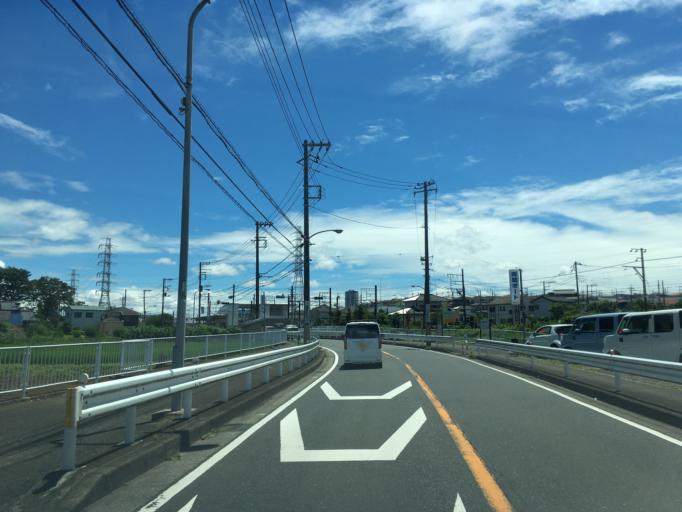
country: JP
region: Tokyo
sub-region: Machida-shi
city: Machida
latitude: 35.5474
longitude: 139.4913
